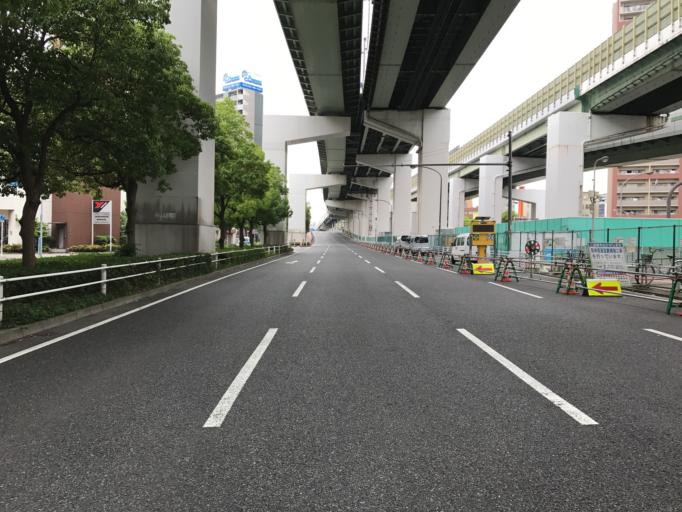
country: JP
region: Osaka
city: Osaka-shi
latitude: 34.6810
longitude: 135.4861
